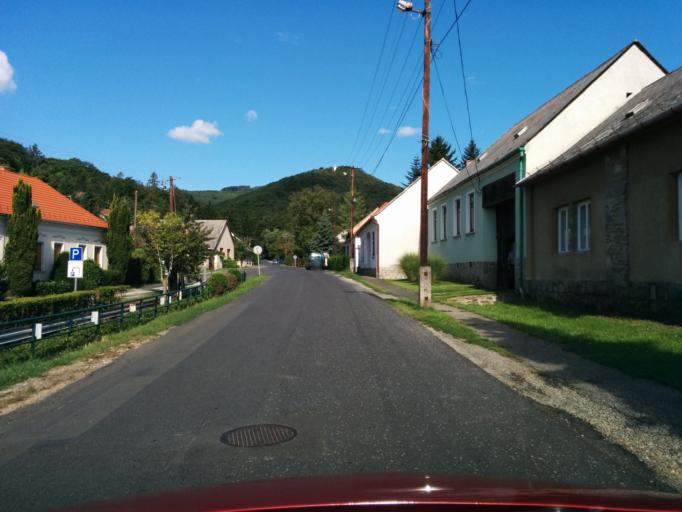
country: HU
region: Vas
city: Koszeg
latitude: 47.3449
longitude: 16.4935
